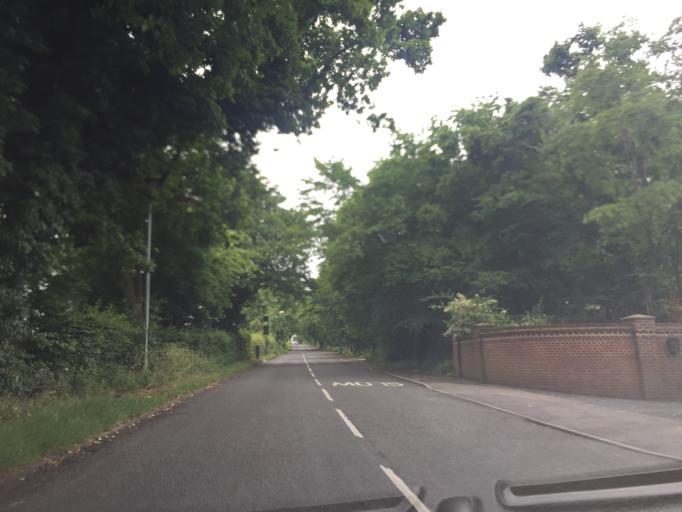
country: GB
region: England
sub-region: Essex
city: Harlow
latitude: 51.7456
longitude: 0.0956
